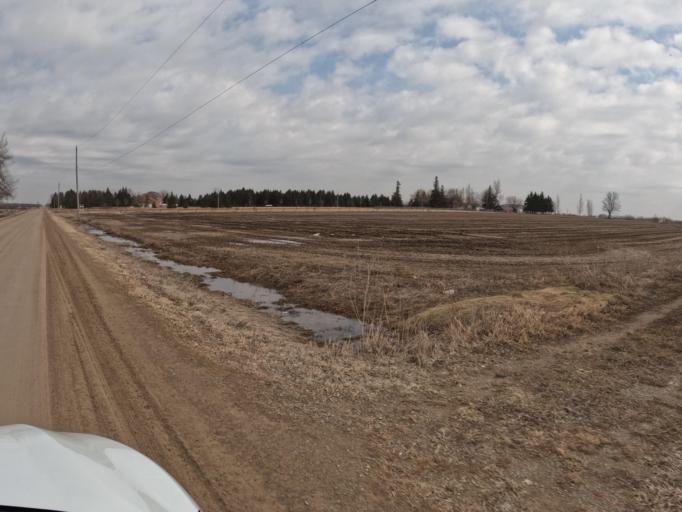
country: CA
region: Ontario
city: Orangeville
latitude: 43.9111
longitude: -80.2157
